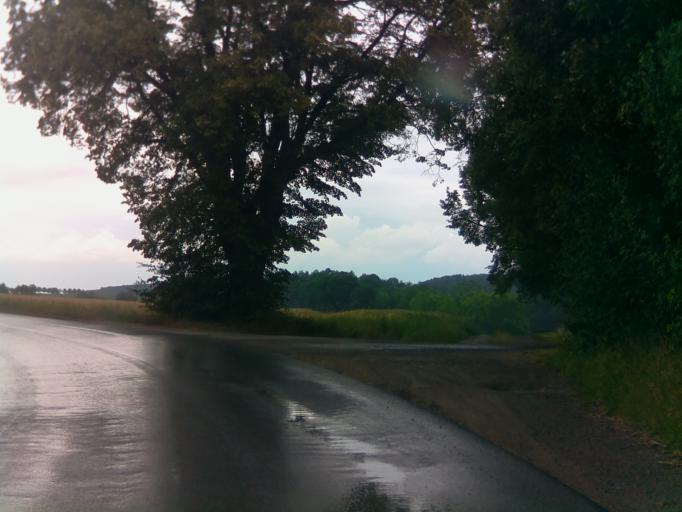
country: DE
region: Thuringia
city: Stadtilm
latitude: 50.7447
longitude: 11.0778
